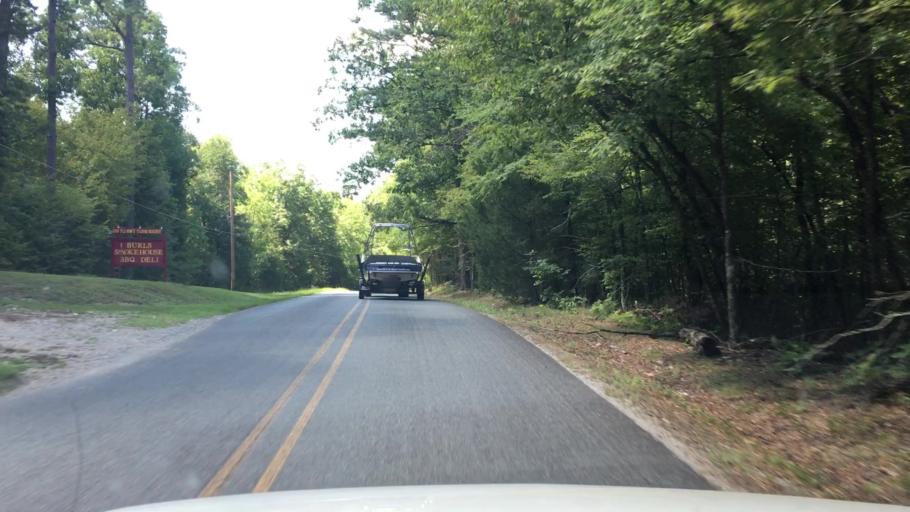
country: US
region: Arkansas
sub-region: Garland County
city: Piney
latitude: 34.5327
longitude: -93.3385
